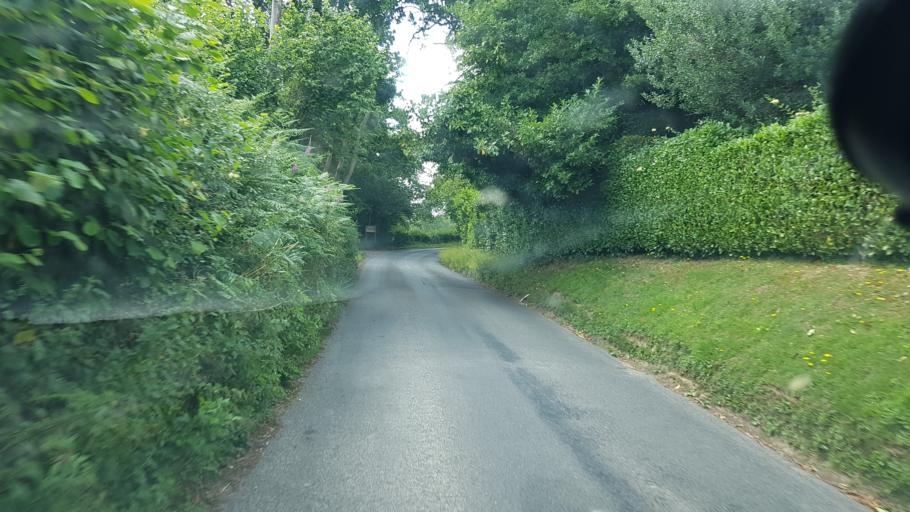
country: GB
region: England
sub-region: West Sussex
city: Maidenbower
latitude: 51.0648
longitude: -0.1522
